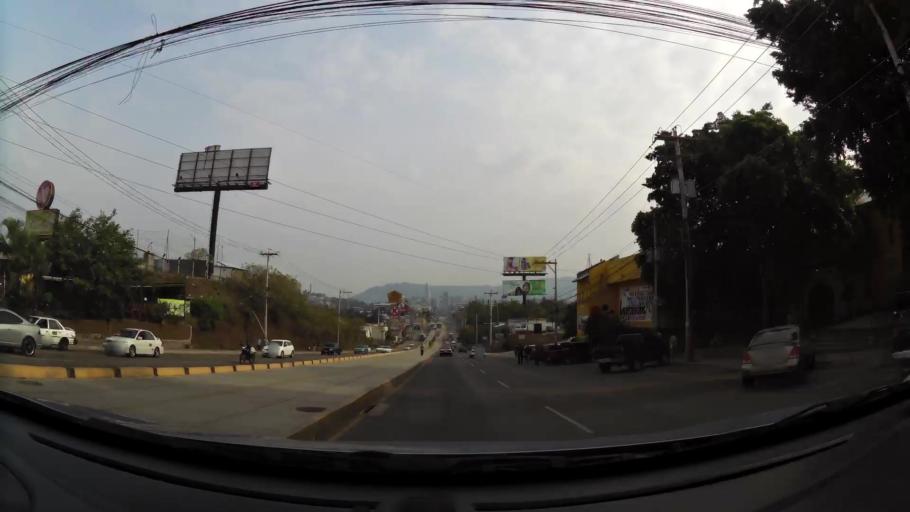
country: HN
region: Francisco Morazan
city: Tegucigalpa
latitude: 14.0695
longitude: -87.1843
